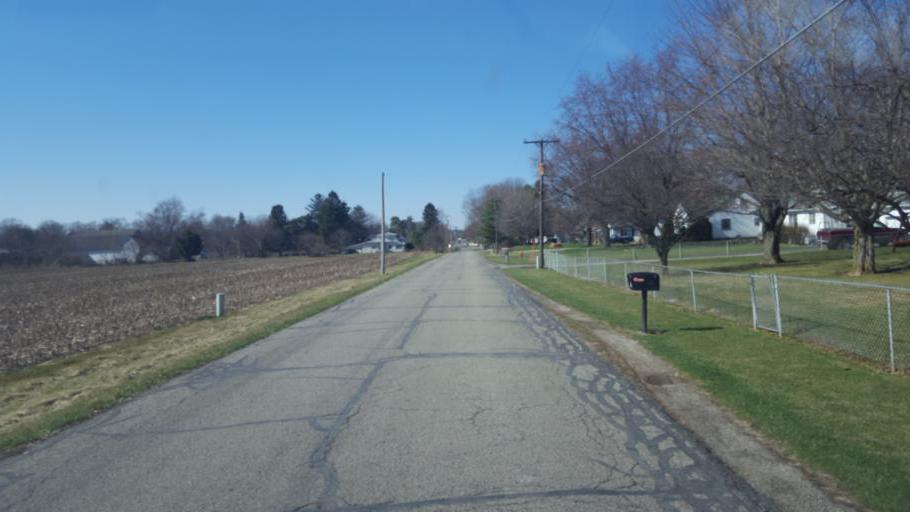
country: US
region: Ohio
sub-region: Morrow County
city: Cardington
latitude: 40.5006
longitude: -82.8835
